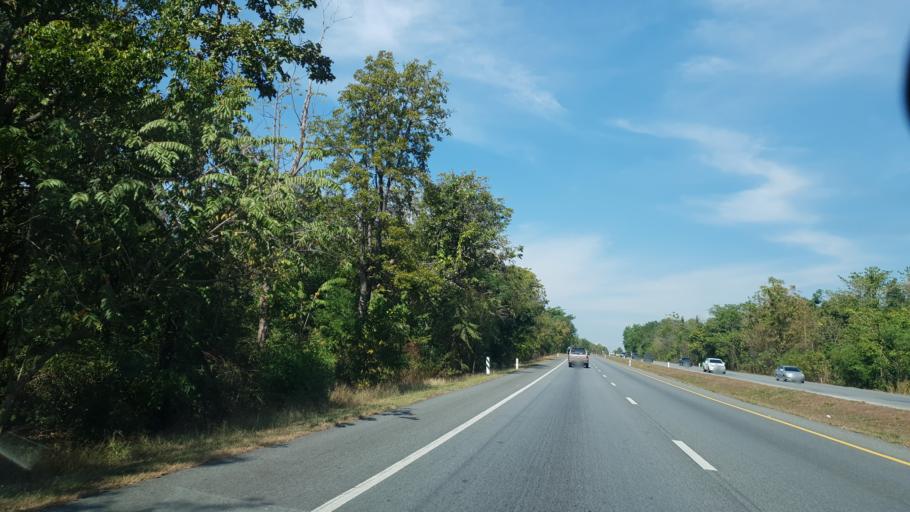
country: TH
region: Uttaradit
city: Thong Saen Khan
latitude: 17.4180
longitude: 100.2270
